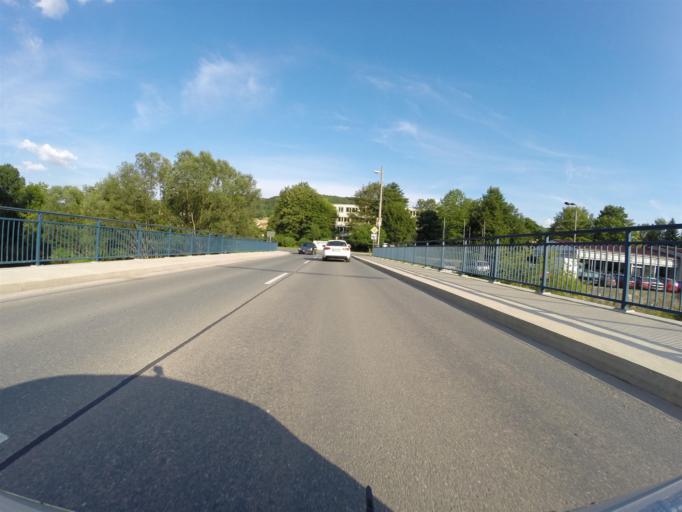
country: DE
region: Thuringia
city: Wichmar
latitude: 51.0089
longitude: 11.6783
